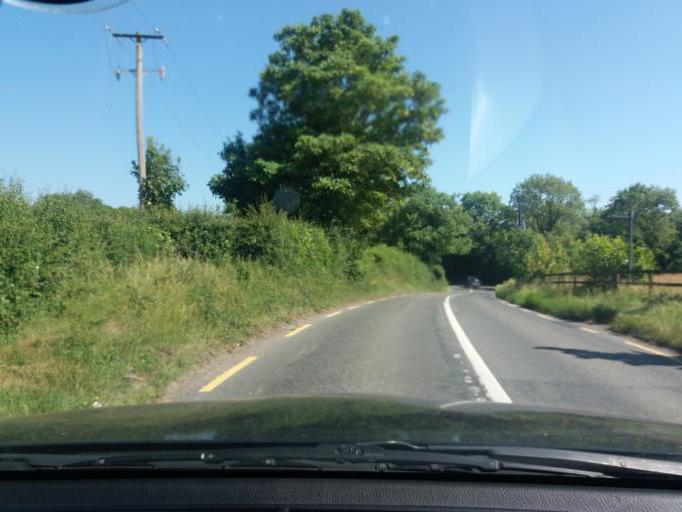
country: IE
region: Leinster
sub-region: Fingal County
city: Swords
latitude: 53.4784
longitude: -6.2747
